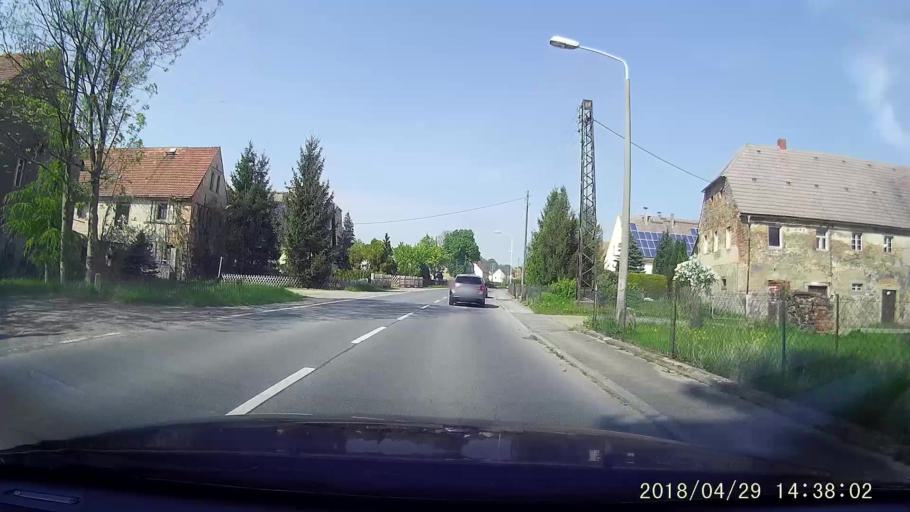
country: DE
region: Saxony
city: Ostritz
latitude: 51.0372
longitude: 14.9438
